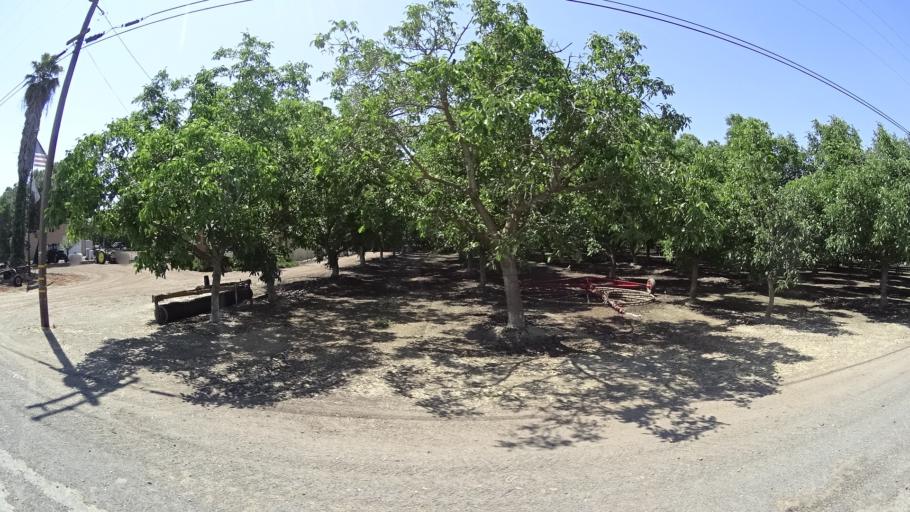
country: US
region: California
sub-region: Fresno County
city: Laton
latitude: 36.4020
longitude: -119.7659
